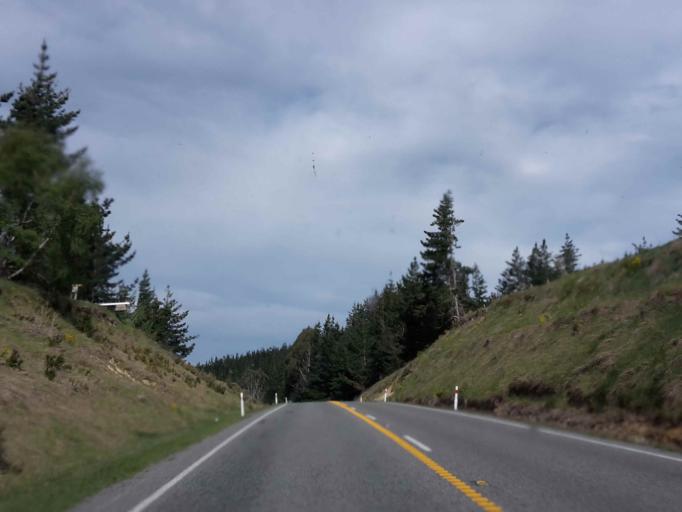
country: NZ
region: Canterbury
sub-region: Timaru District
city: Pleasant Point
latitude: -44.1234
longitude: 171.0733
